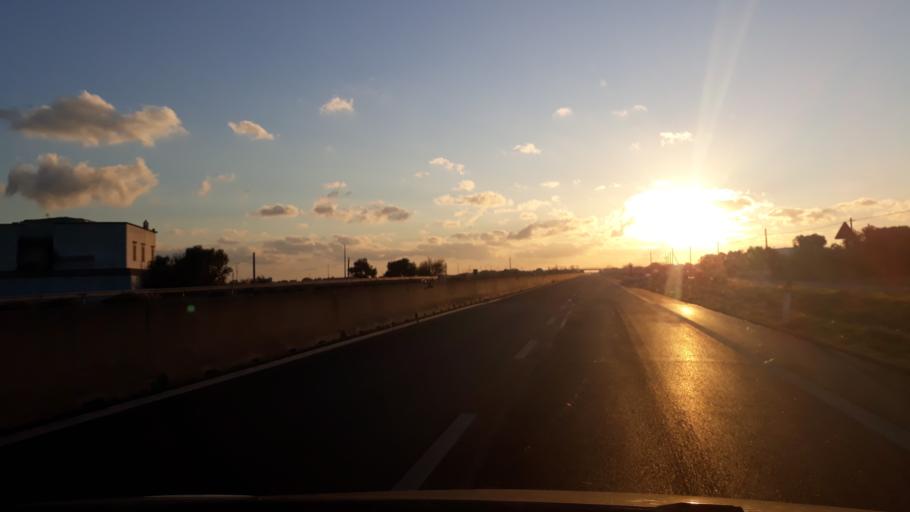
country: IT
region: Apulia
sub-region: Provincia di Brindisi
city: Ostuni
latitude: 40.7763
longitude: 17.6072
